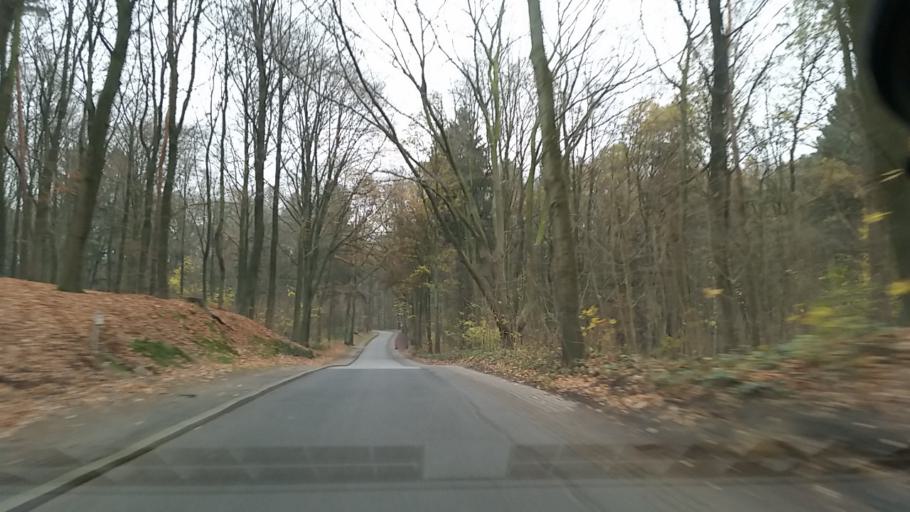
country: DE
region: Schleswig-Holstein
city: Rellingen
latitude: 53.5751
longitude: 9.7905
